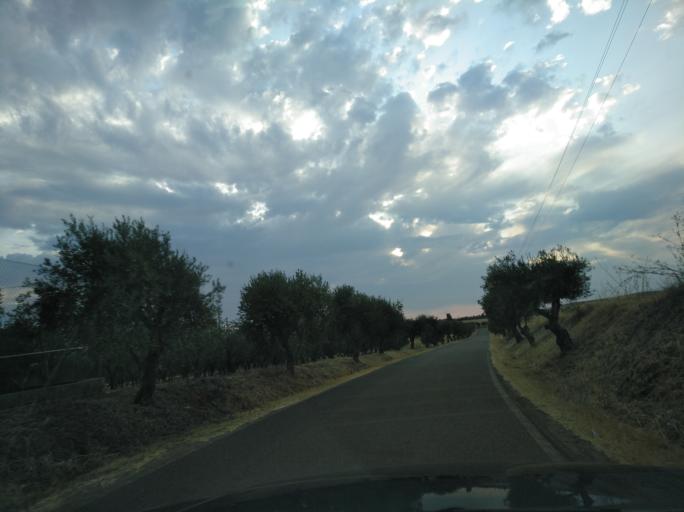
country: PT
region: Portalegre
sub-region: Campo Maior
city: Campo Maior
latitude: 39.0159
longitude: -7.0338
